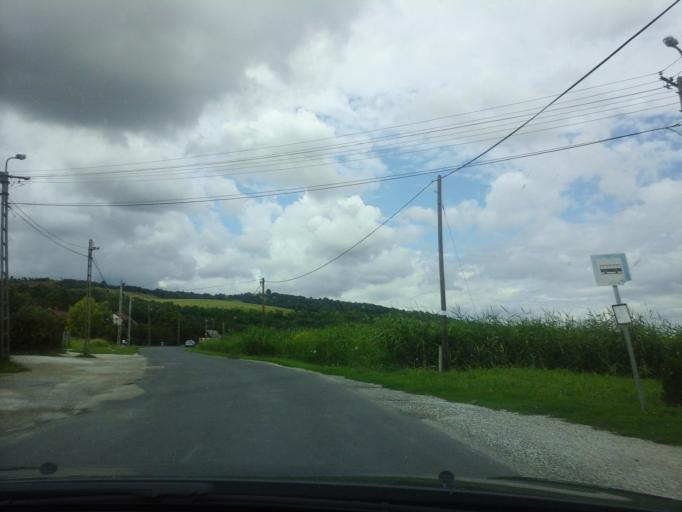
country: HU
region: Borsod-Abauj-Zemplen
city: Izsofalva
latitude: 48.3031
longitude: 20.6350
